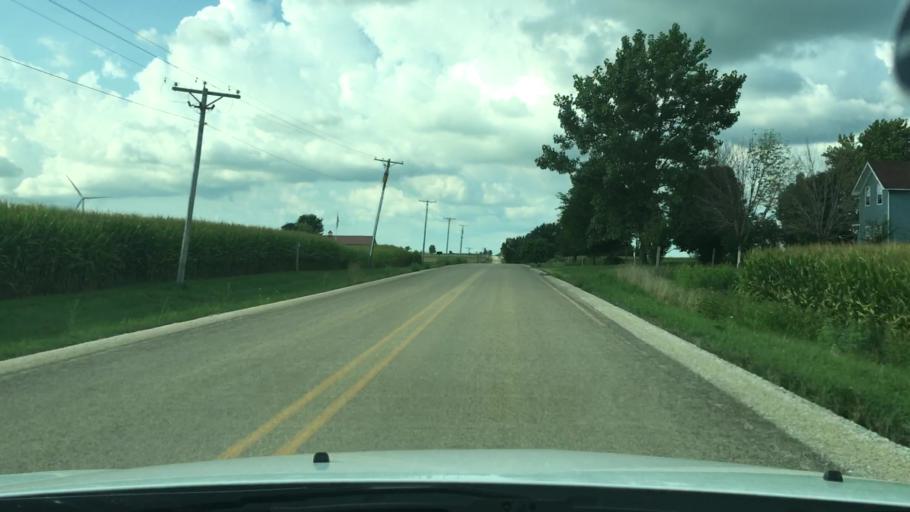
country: US
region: Illinois
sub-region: DeKalb County
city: Waterman
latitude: 41.8105
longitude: -88.7733
